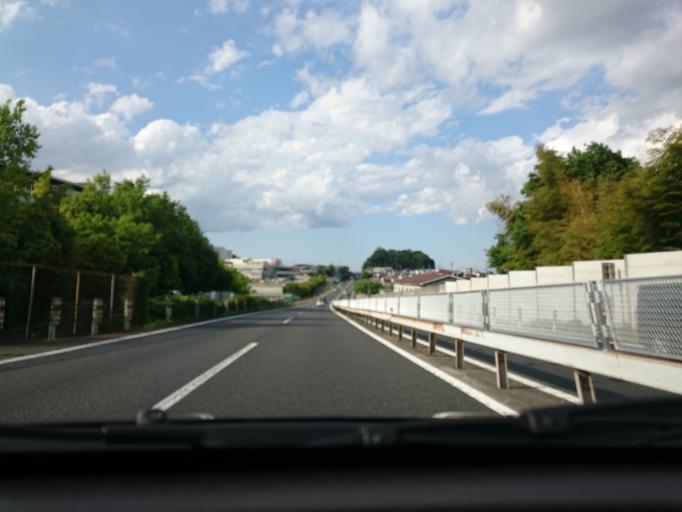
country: JP
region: Kanagawa
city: Oiso
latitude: 35.3469
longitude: 139.2972
